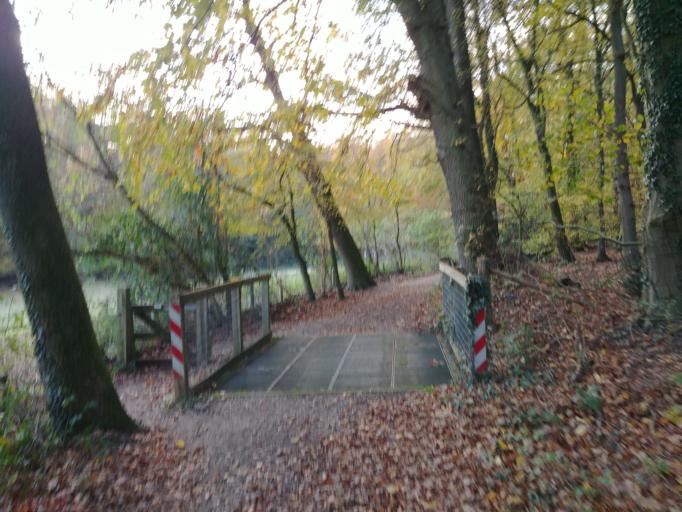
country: NL
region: Gelderland
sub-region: Gemeente Rheden
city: De Steeg
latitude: 52.0240
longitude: 6.0560
